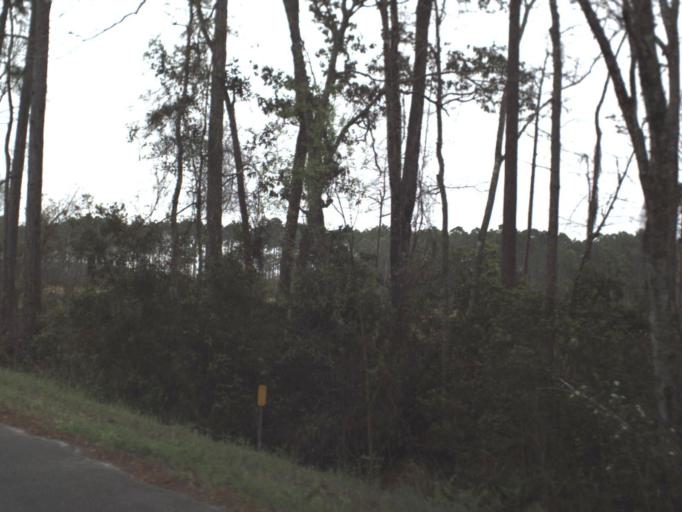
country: US
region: Florida
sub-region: Franklin County
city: Eastpoint
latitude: 29.8226
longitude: -84.9080
